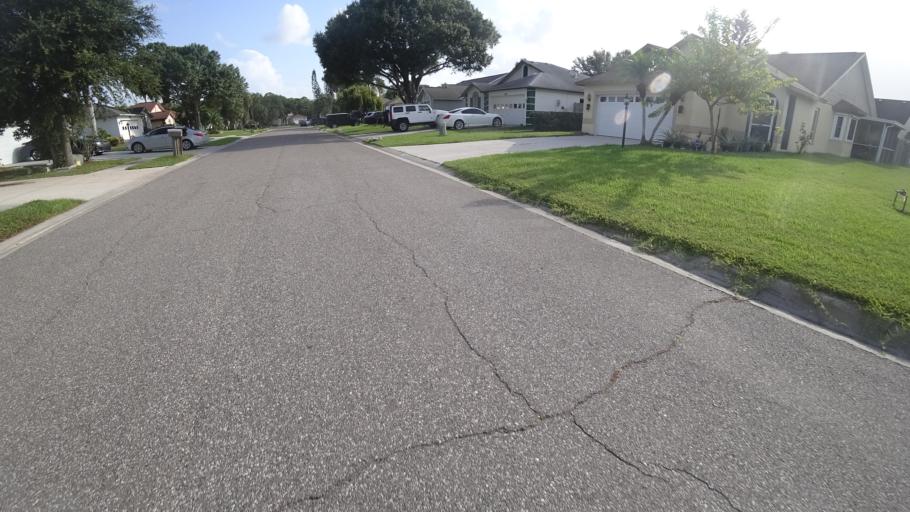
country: US
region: Florida
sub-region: Sarasota County
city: North Sarasota
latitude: 27.4158
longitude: -82.5075
